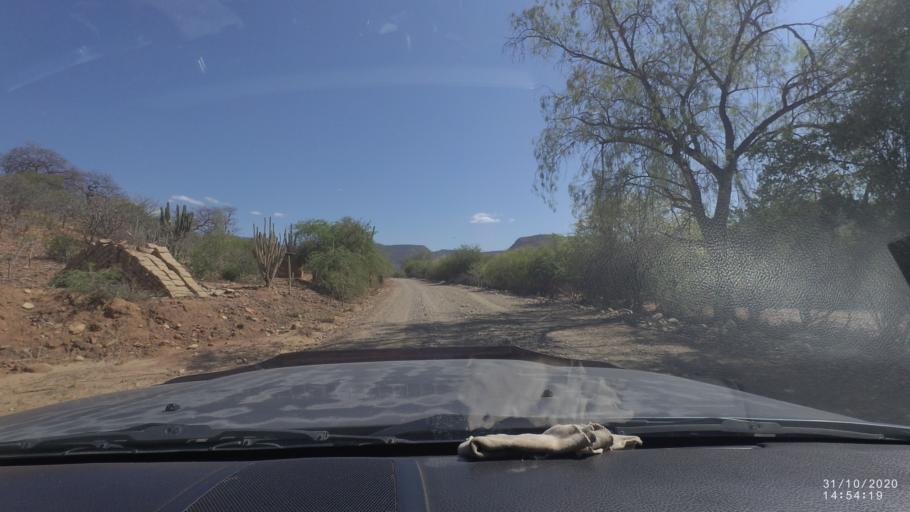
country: BO
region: Cochabamba
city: Aiquile
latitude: -18.2251
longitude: -64.8574
